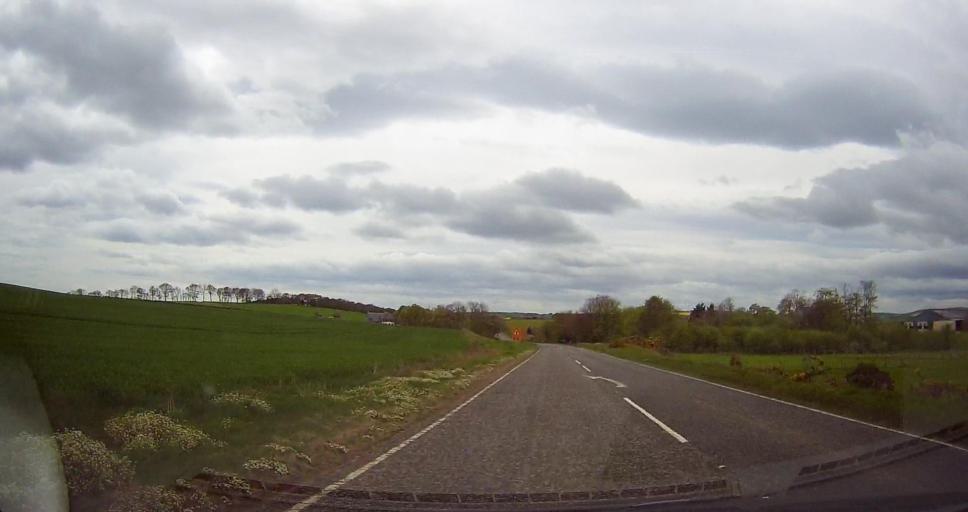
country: GB
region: Scotland
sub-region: Aberdeenshire
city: Stonehaven
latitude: 56.9143
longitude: -2.2155
